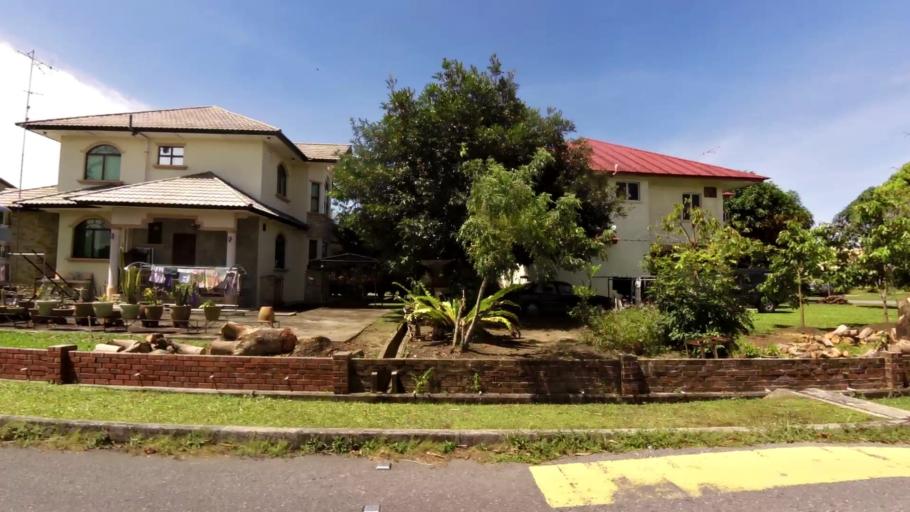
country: BN
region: Belait
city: Kuala Belait
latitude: 4.5866
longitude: 114.2261
